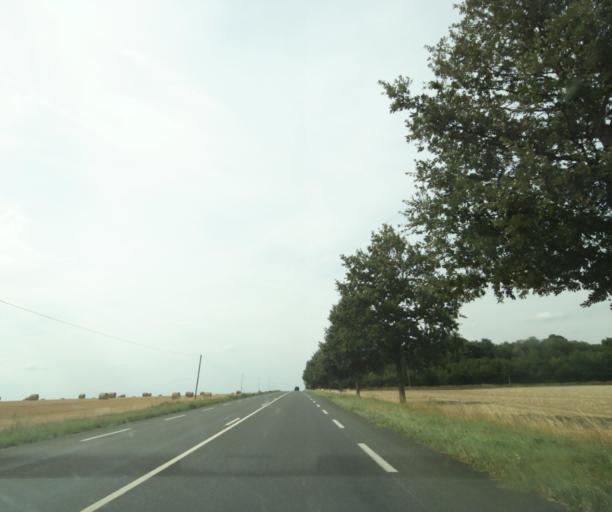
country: FR
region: Centre
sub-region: Departement d'Indre-et-Loire
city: Saint-Christophe-sur-le-Nais
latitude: 47.6511
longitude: 0.4925
